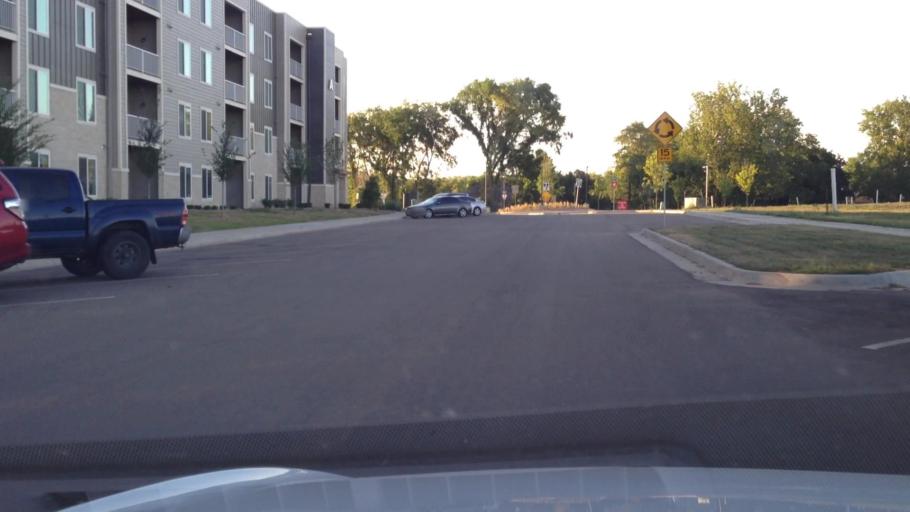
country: US
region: Kansas
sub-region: Douglas County
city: Lawrence
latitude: 38.9536
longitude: -95.2920
